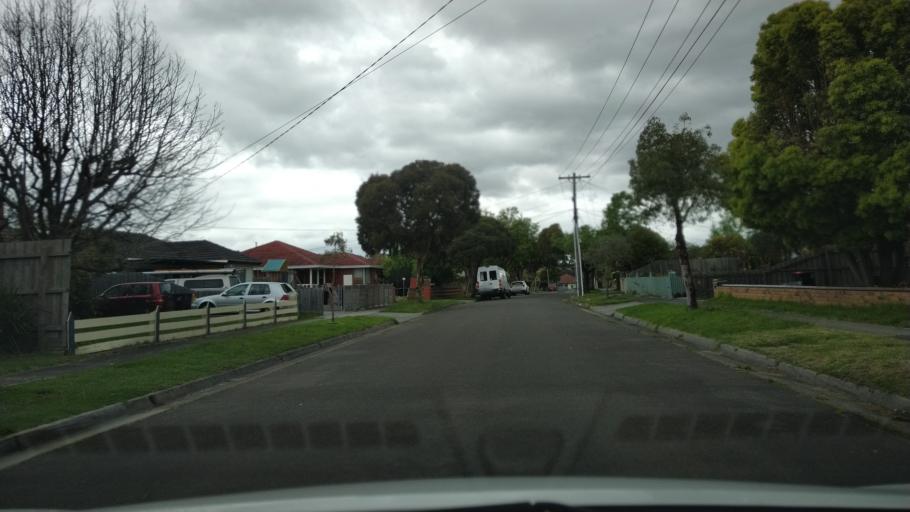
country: AU
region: Victoria
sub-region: Greater Dandenong
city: Noble Park
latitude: -37.9729
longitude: 145.1807
